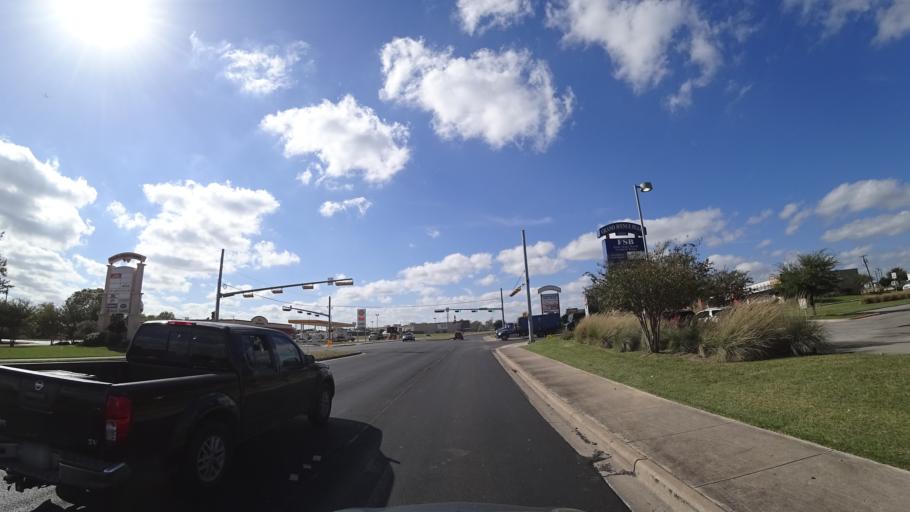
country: US
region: Texas
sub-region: Travis County
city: Windemere
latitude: 30.4562
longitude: -97.6592
